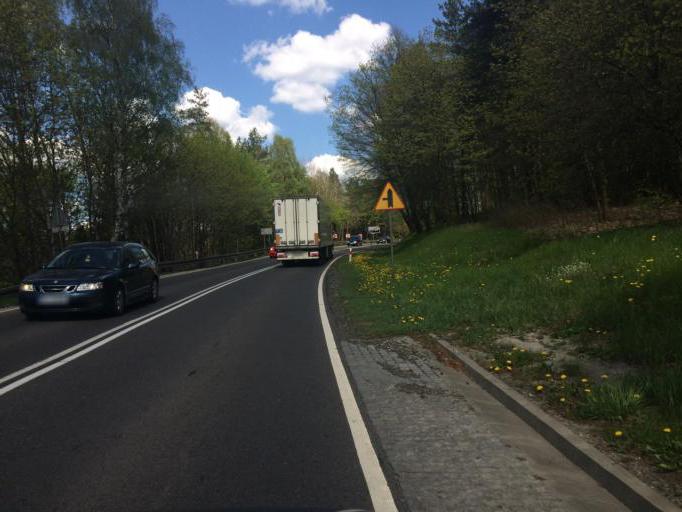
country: PL
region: Warmian-Masurian Voivodeship
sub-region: Powiat olsztynski
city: Gietrzwald
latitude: 53.7266
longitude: 20.1497
